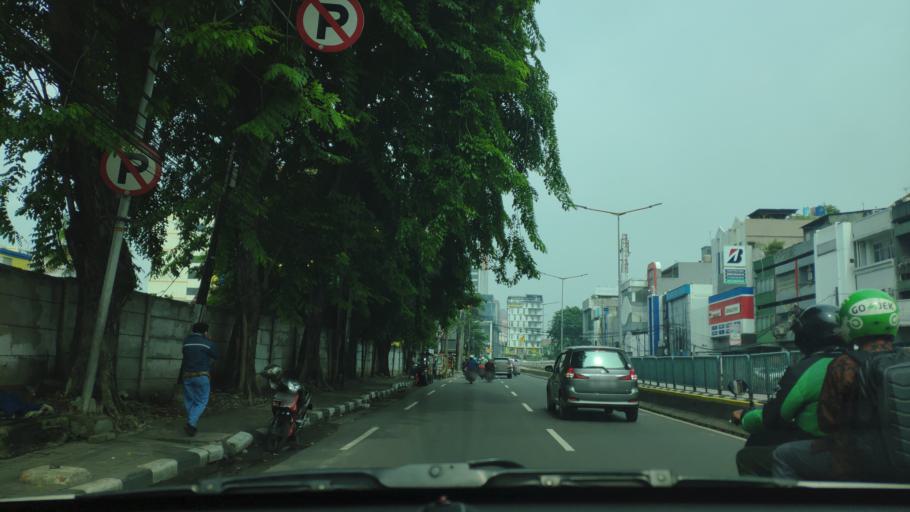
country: ID
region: Jakarta Raya
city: Jakarta
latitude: -6.1650
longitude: 106.8173
